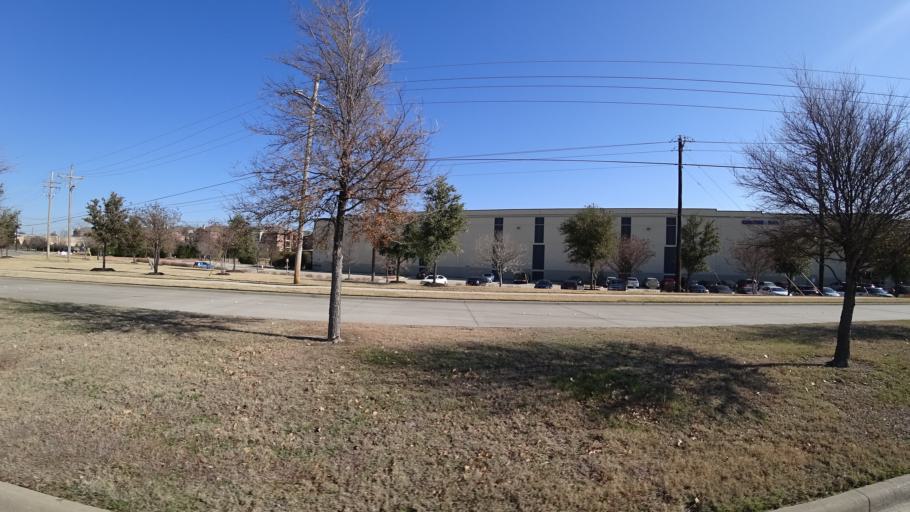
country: US
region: Texas
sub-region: Dallas County
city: Coppell
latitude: 33.0012
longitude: -97.0162
